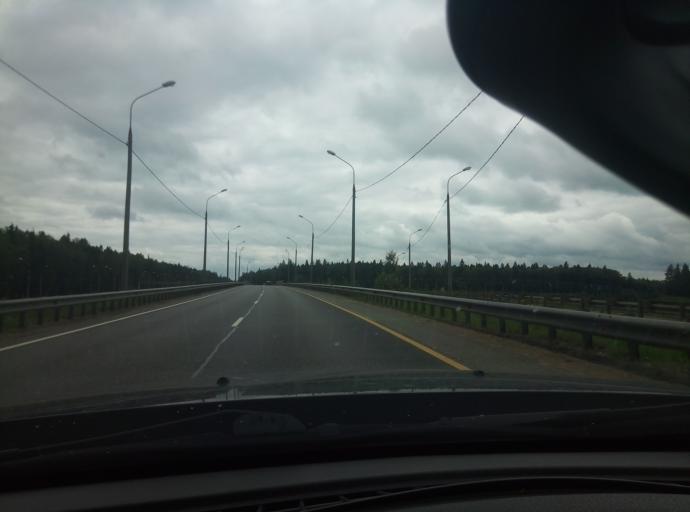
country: RU
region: Kaluga
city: Maloyaroslavets
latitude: 54.9801
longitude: 36.4935
